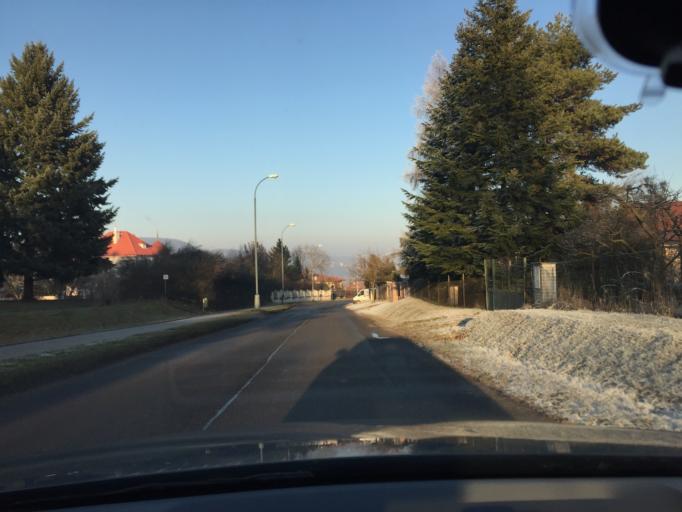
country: CZ
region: Central Bohemia
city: Cernosice
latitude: 49.9517
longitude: 14.3166
